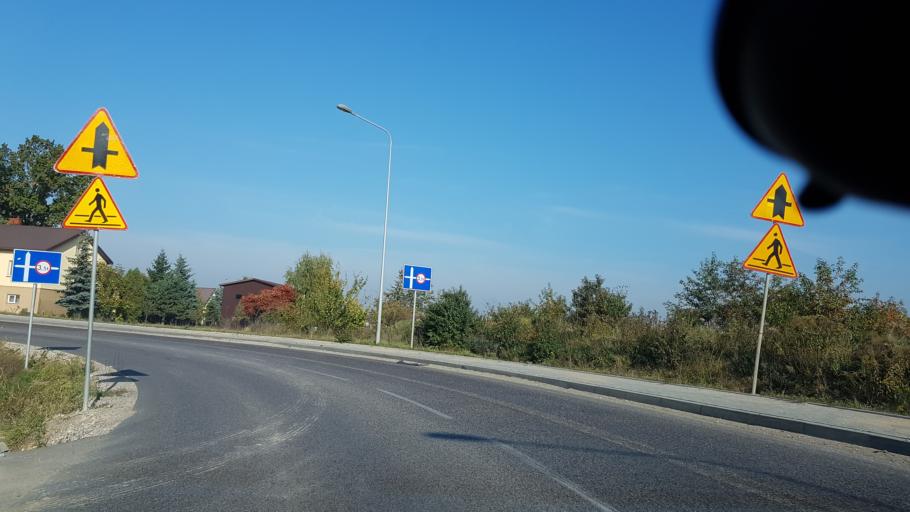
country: PL
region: Masovian Voivodeship
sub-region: Powiat pruszkowski
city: Nadarzyn
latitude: 52.0766
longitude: 20.7730
